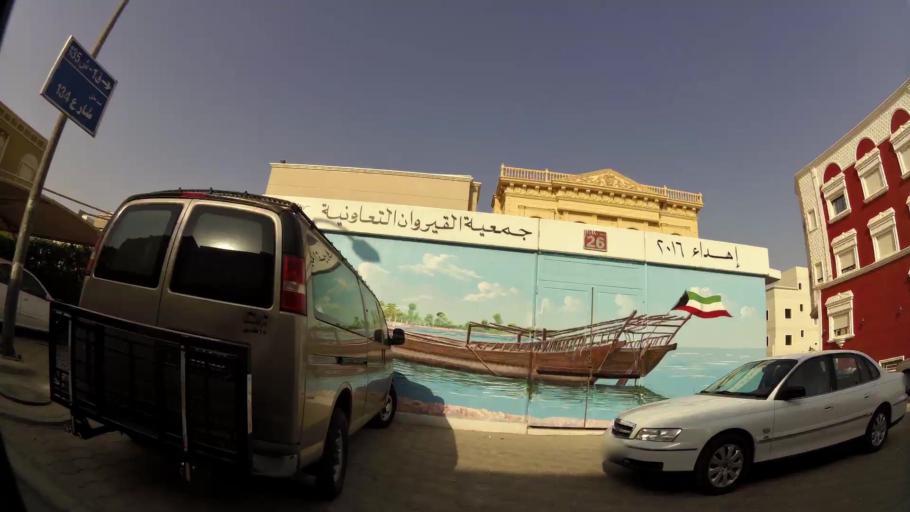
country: KW
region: Al Asimah
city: Ar Rabiyah
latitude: 29.3020
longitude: 47.8064
